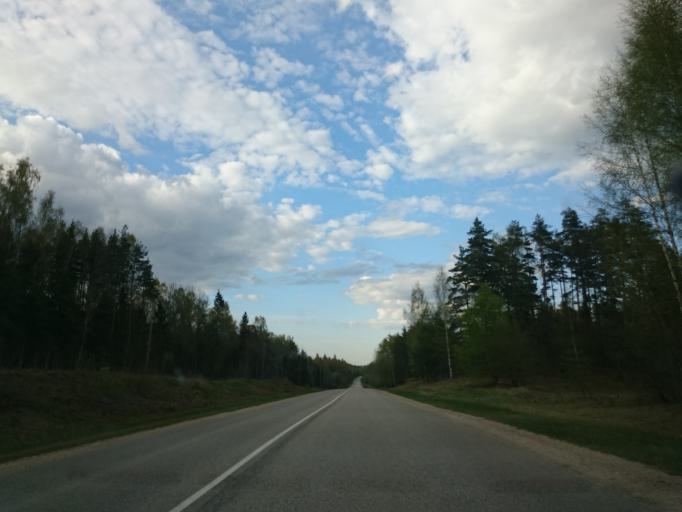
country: LV
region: Kuldigas Rajons
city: Kuldiga
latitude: 56.9410
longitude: 21.9317
